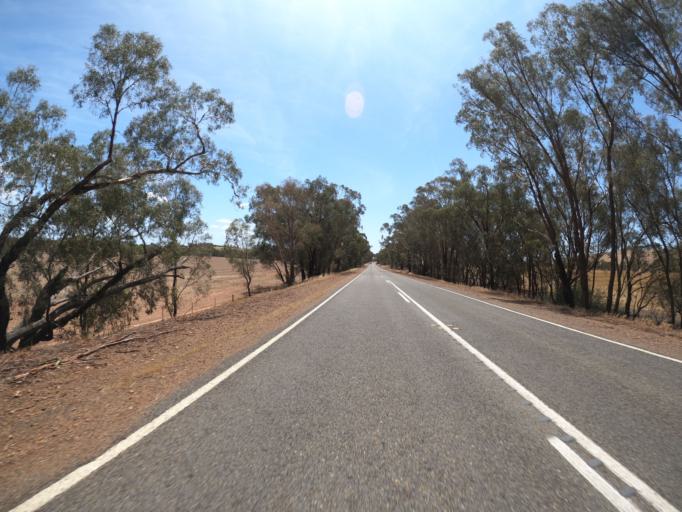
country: AU
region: Victoria
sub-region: Benalla
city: Benalla
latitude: -36.3472
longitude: 145.9611
